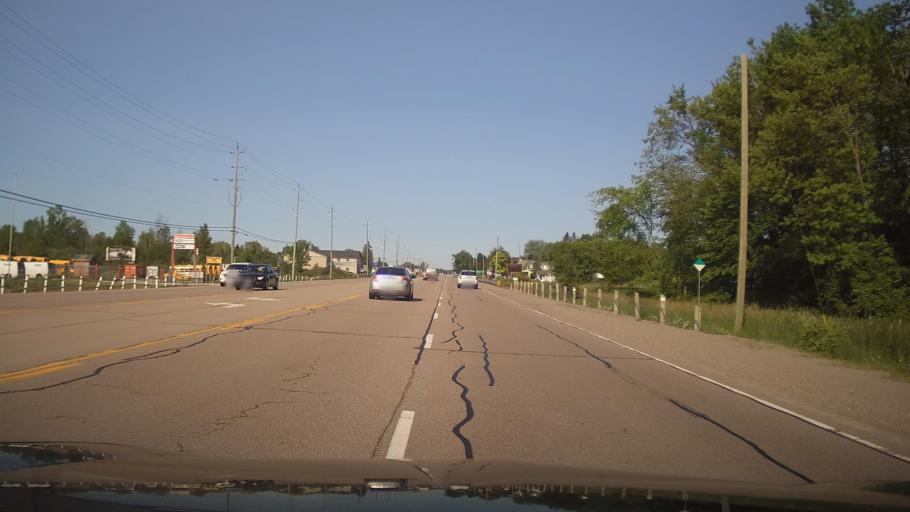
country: CA
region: Ontario
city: Peterborough
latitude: 44.3016
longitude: -78.2505
